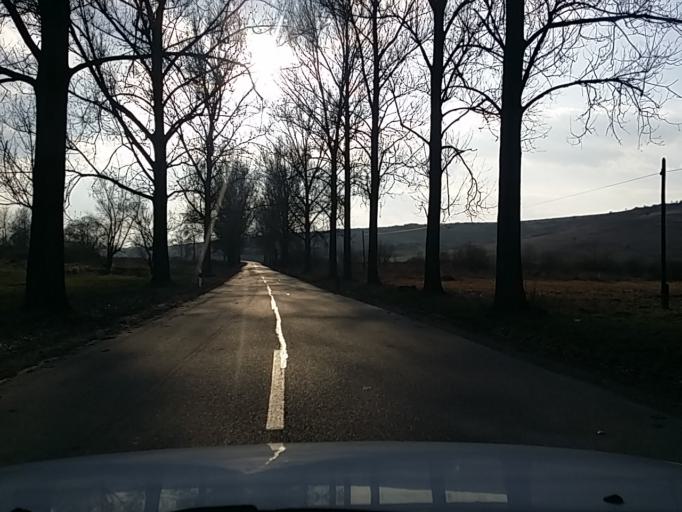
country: HU
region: Borsod-Abauj-Zemplen
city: Putnok
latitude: 48.3519
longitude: 20.4203
